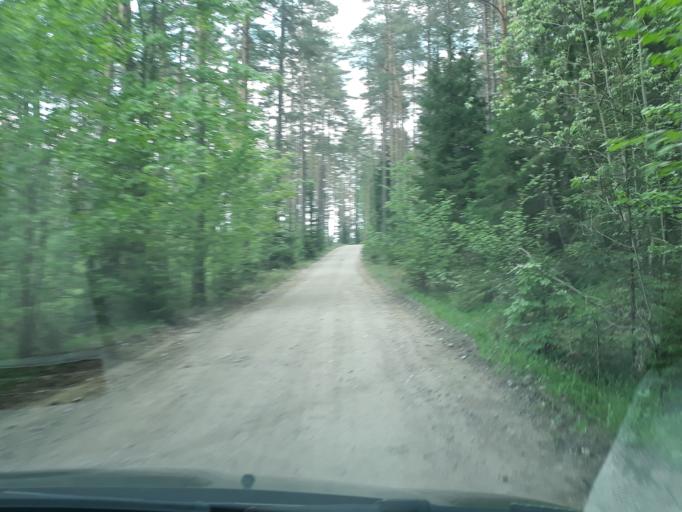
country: LV
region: Ligatne
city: Ligatne
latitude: 57.2710
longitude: 24.9861
